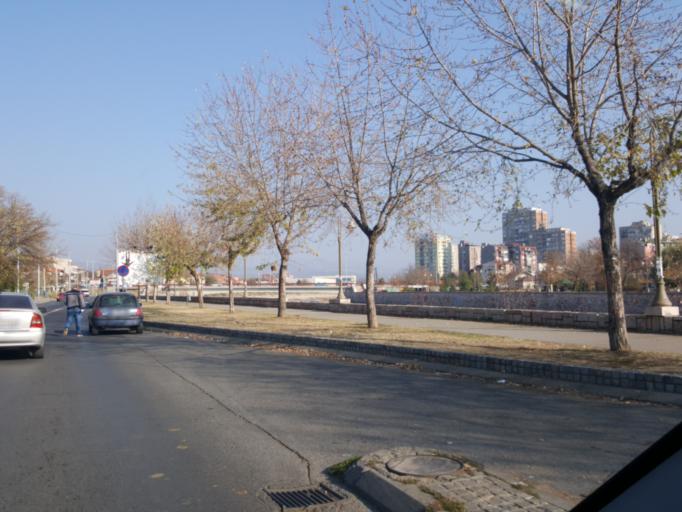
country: RS
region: Central Serbia
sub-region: Nisavski Okrug
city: Nis
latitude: 43.3259
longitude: 21.8997
